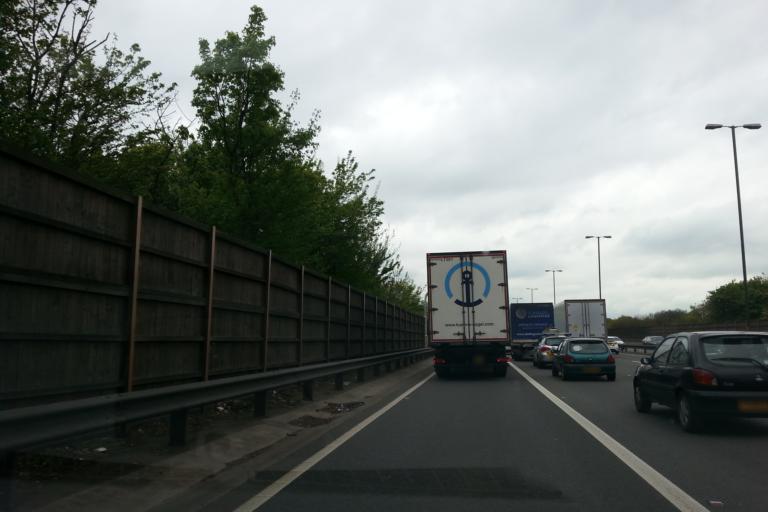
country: GB
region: England
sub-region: City and Borough of Birmingham
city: Hockley
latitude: 52.5455
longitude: -1.9170
